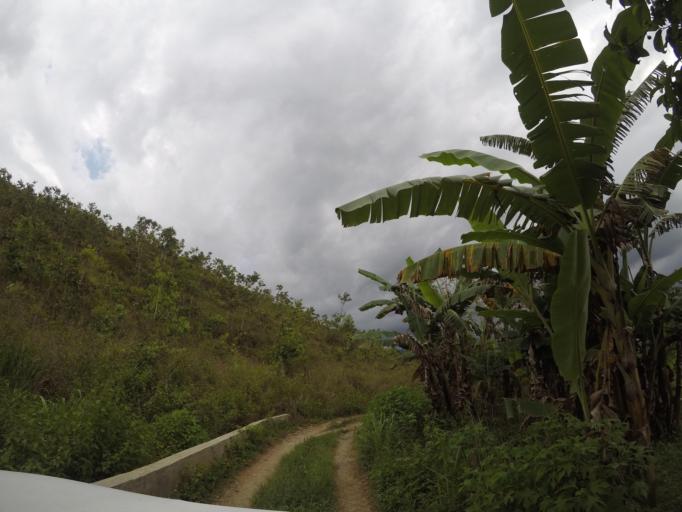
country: TL
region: Ermera
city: Gleno
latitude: -8.7075
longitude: 125.4519
